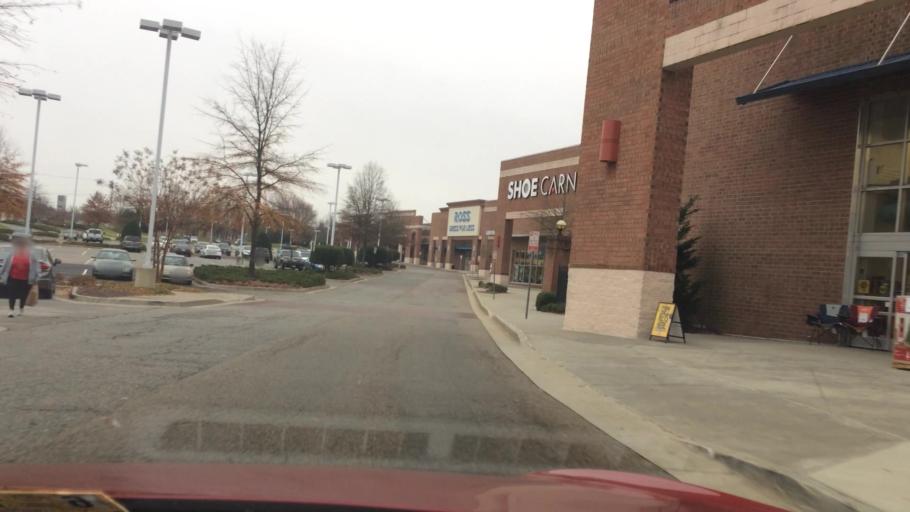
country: US
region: Virginia
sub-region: Henrico County
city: Glen Allen
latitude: 37.6697
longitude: -77.4634
